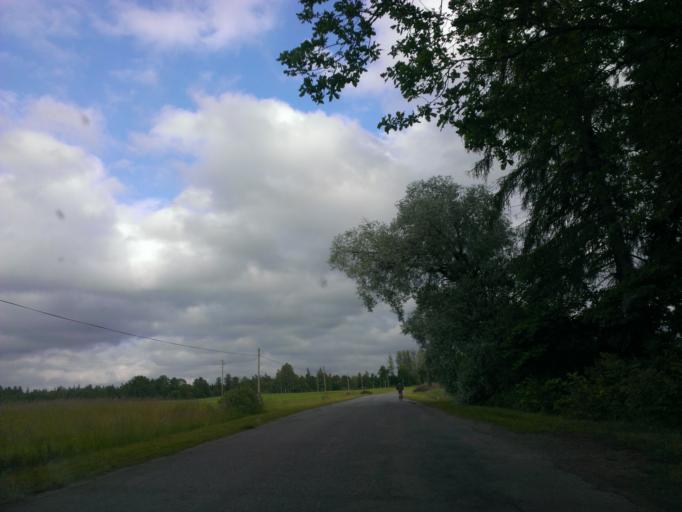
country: LV
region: Aizpute
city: Aizpute
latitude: 56.7227
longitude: 21.7523
